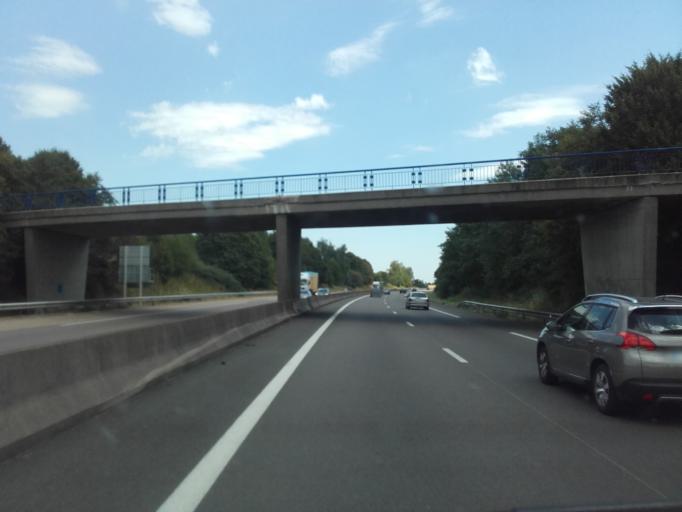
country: FR
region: Bourgogne
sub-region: Departement de la Cote-d'Or
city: Semur-en-Auxois
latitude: 47.4473
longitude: 4.2880
